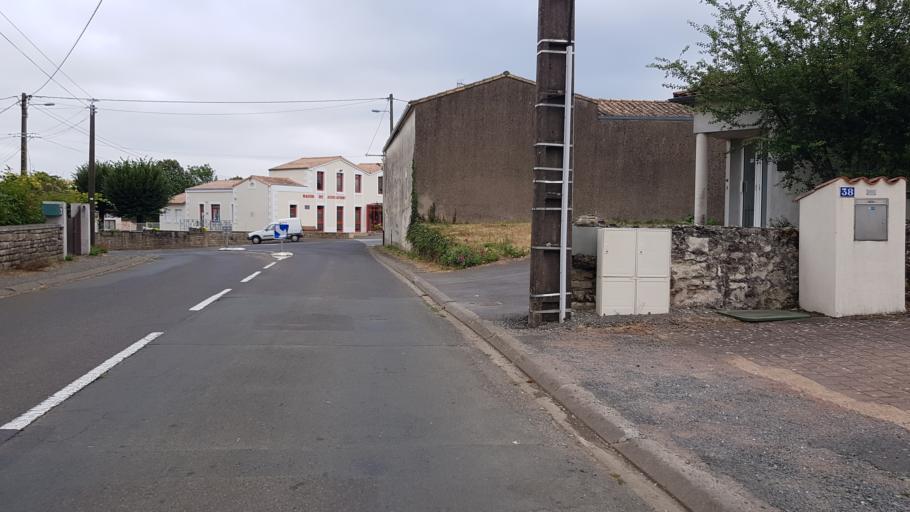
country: FR
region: Poitou-Charentes
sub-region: Departement des Deux-Sevres
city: Vouille
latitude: 46.3172
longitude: -0.3632
